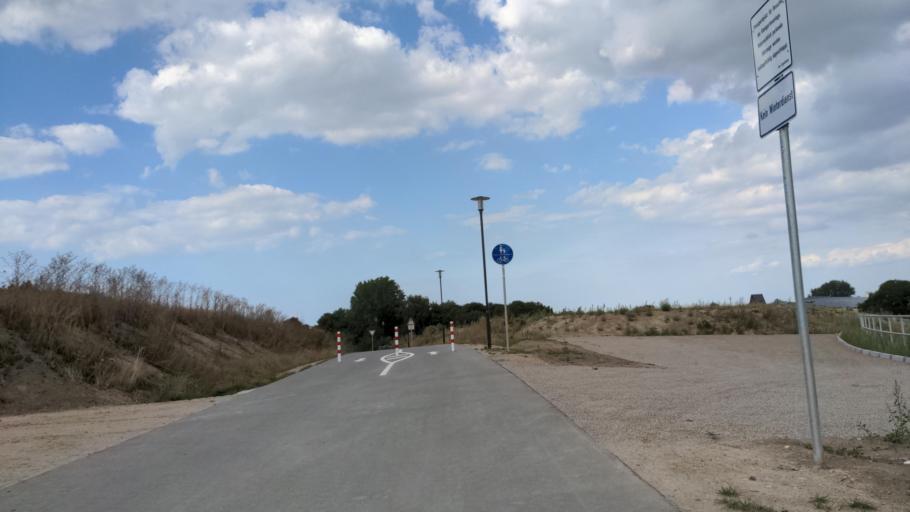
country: DE
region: Mecklenburg-Vorpommern
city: Wismar
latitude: 53.8980
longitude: 11.4281
